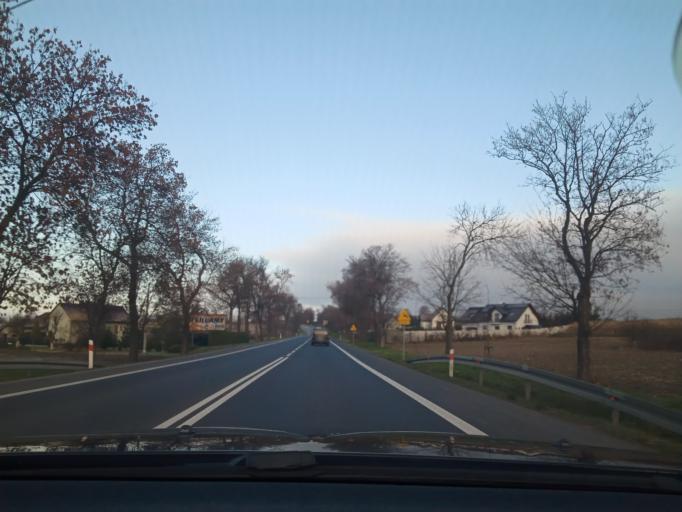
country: PL
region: Lesser Poland Voivodeship
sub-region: Powiat krakowski
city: Slomniki
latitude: 50.2875
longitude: 20.0509
